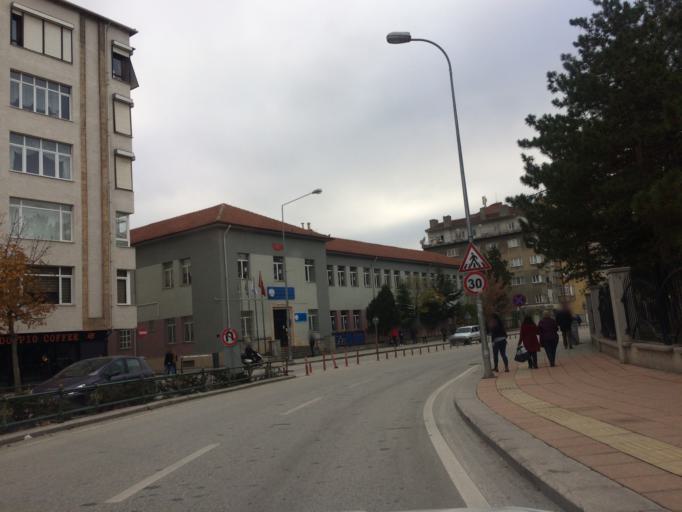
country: TR
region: Eskisehir
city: Eskisehir
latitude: 39.7800
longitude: 30.5112
